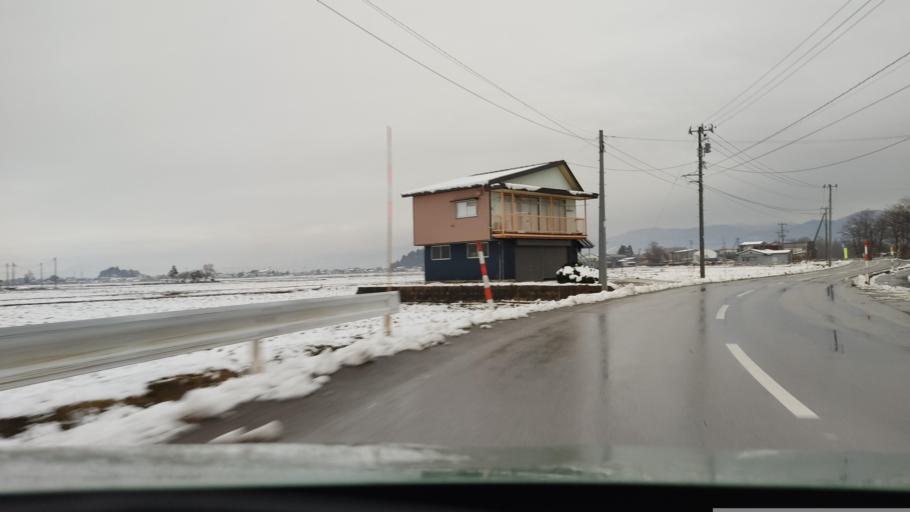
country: JP
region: Akita
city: Omagari
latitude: 39.4584
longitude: 140.5285
